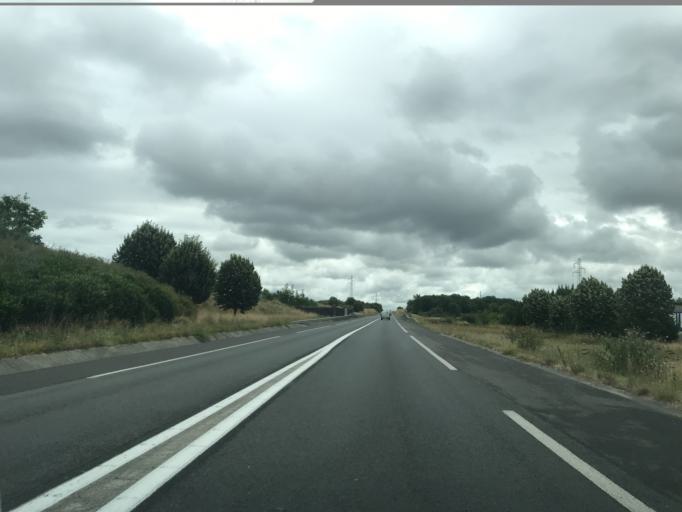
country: FR
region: Poitou-Charentes
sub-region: Departement de la Charente
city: Puymoyen
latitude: 45.6261
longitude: 0.1633
